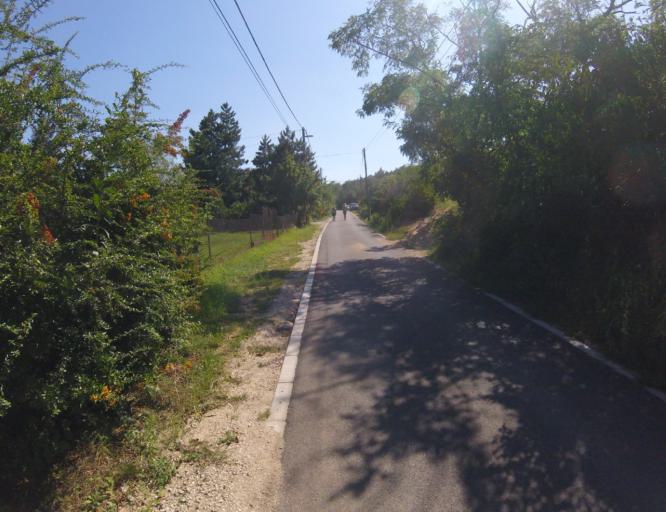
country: HU
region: Fejer
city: Velence
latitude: 47.2521
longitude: 18.6114
